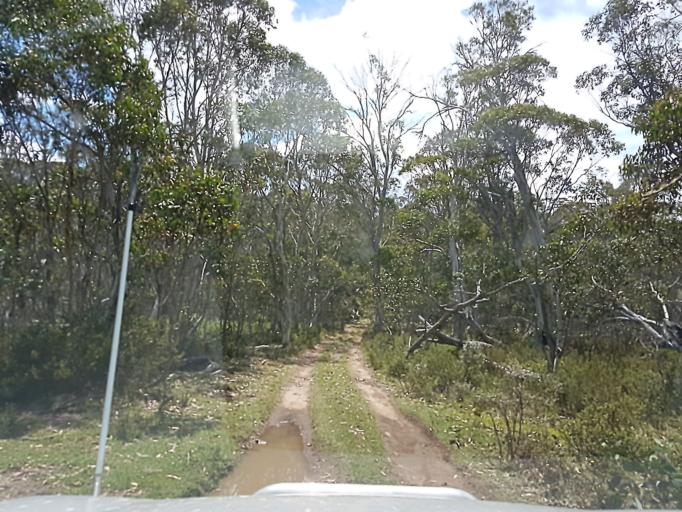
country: AU
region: New South Wales
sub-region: Snowy River
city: Jindabyne
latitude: -36.9172
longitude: 148.1312
